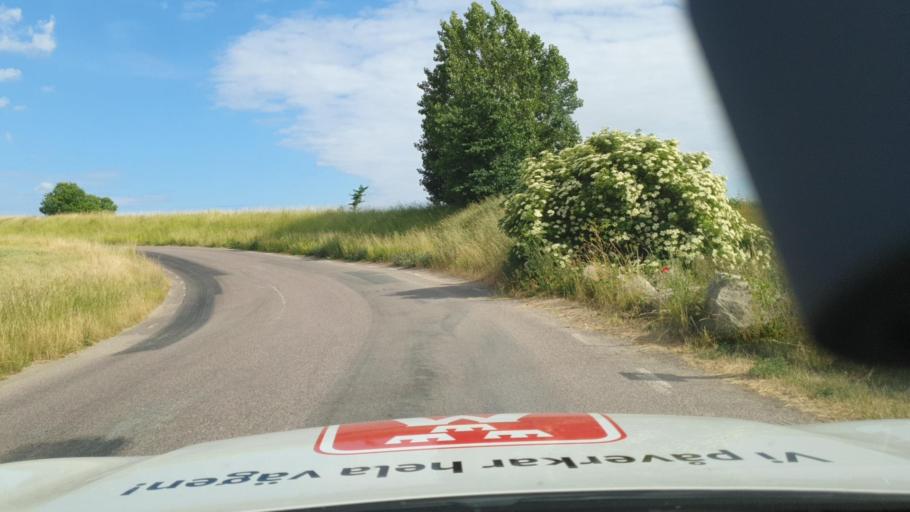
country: SE
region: Skane
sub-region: Skurups Kommun
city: Skurup
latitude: 55.4540
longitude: 13.5348
